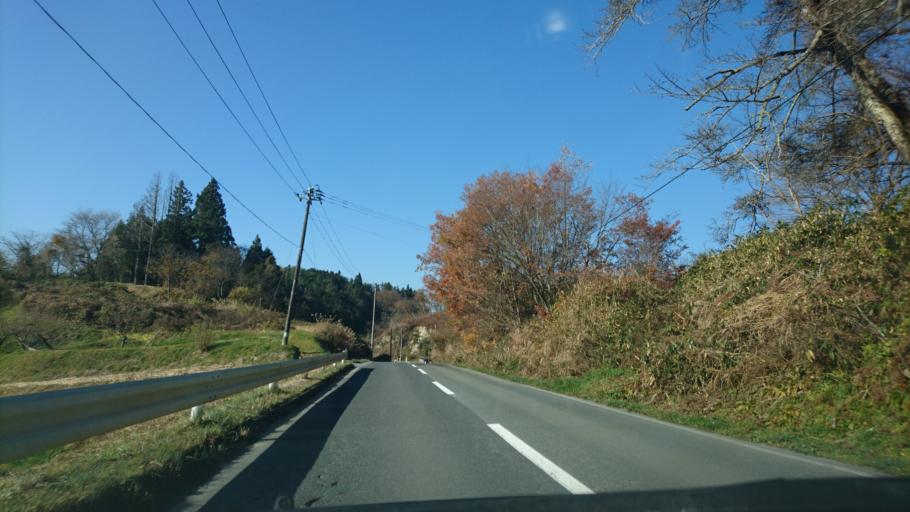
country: JP
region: Iwate
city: Ichinoseki
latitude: 38.9025
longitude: 141.4022
